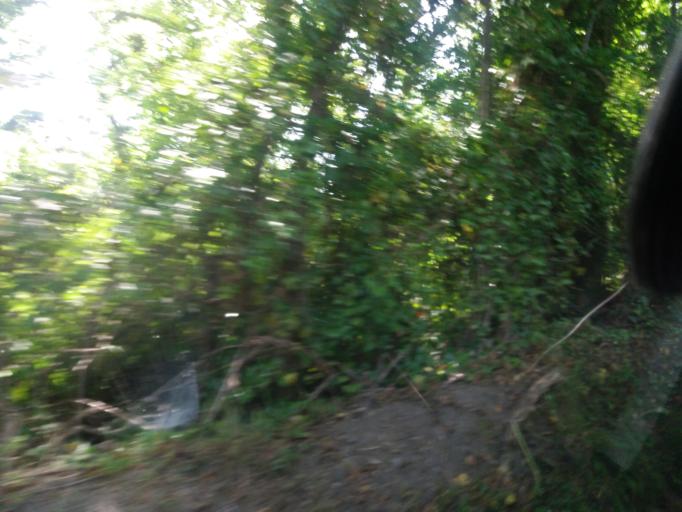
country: IE
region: Leinster
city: Lusk
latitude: 53.5185
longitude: -6.1895
